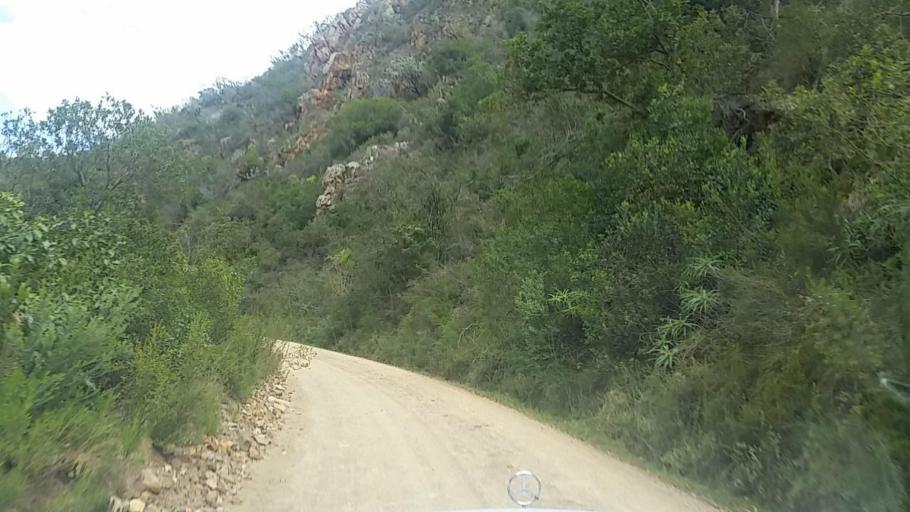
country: ZA
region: Western Cape
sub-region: Eden District Municipality
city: Knysna
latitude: -33.8073
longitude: 23.1803
